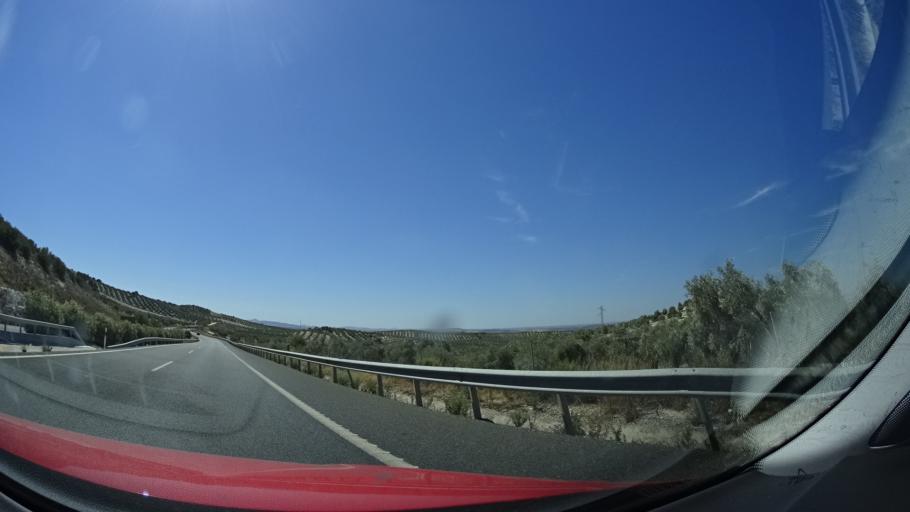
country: ES
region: Andalusia
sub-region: Provincia de Sevilla
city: Estepa
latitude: 37.2881
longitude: -4.9104
